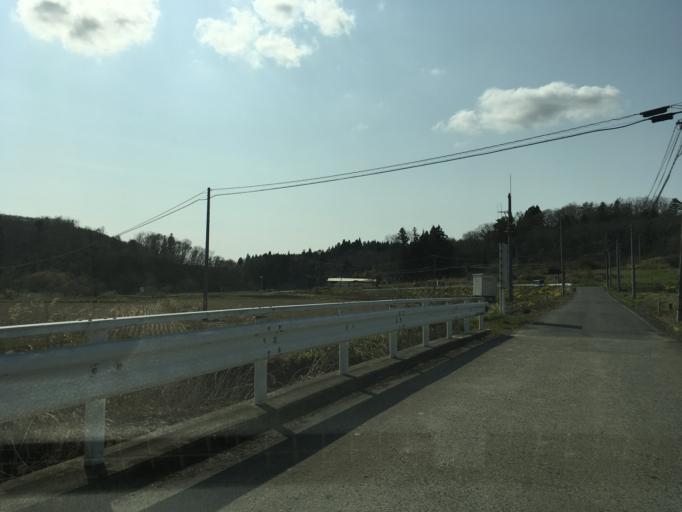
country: JP
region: Iwate
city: Ichinoseki
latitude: 38.8427
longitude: 141.3538
